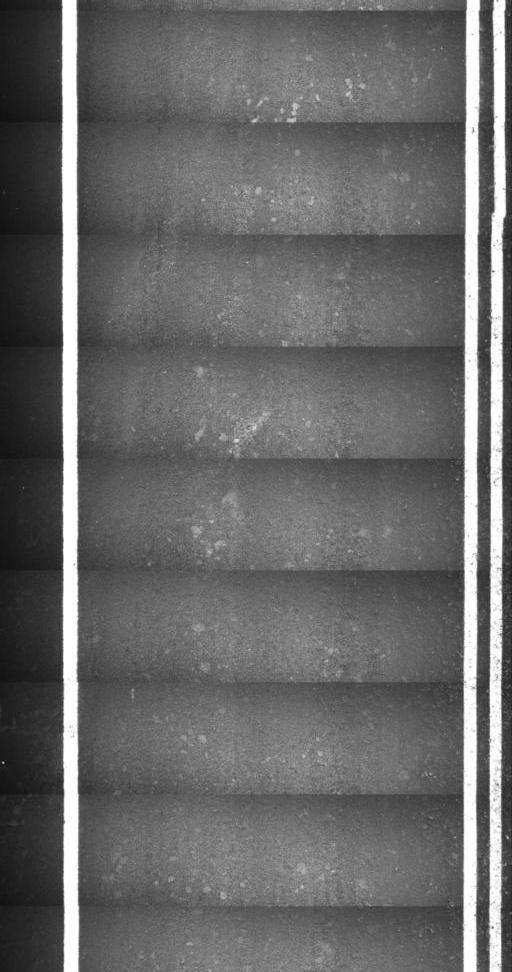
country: US
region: Vermont
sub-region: Orange County
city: Randolph
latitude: 43.9119
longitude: -72.6644
